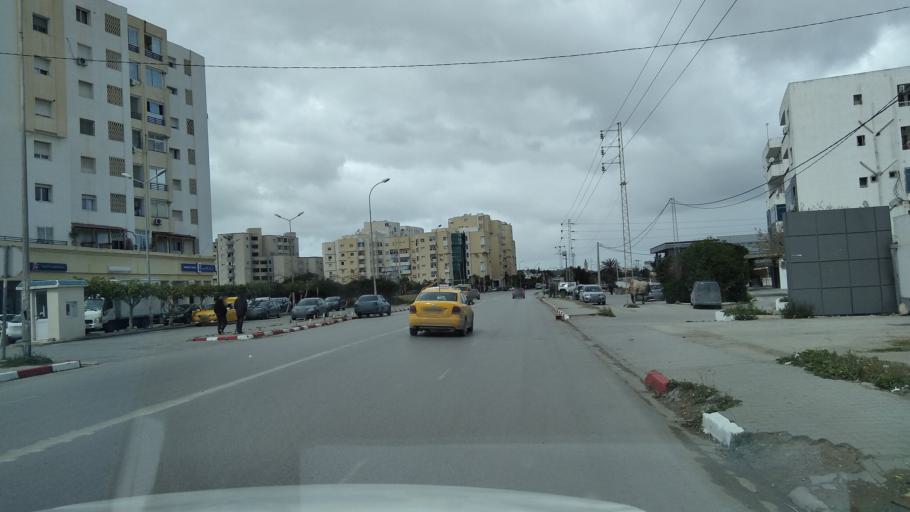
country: TN
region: Bin 'Arus
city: Ben Arous
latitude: 36.7465
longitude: 10.2321
